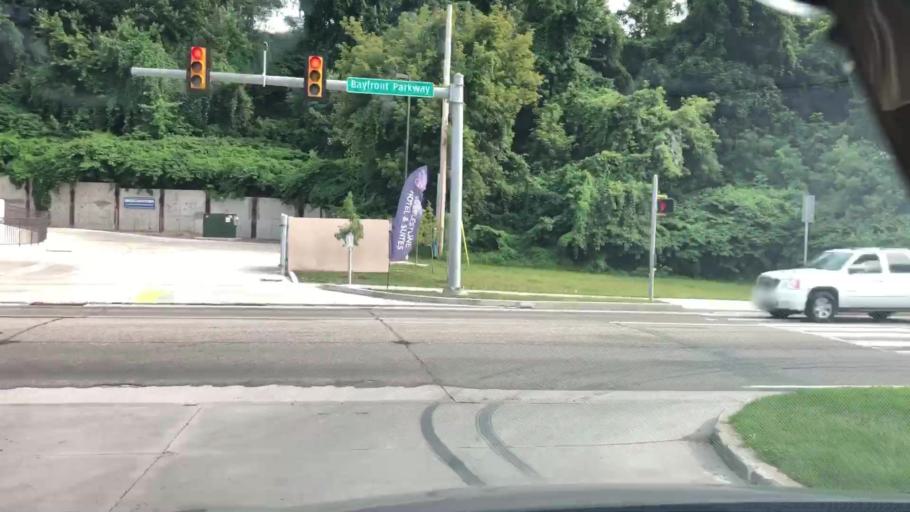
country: US
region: Pennsylvania
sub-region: Erie County
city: Erie
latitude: 42.1283
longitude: -80.1058
